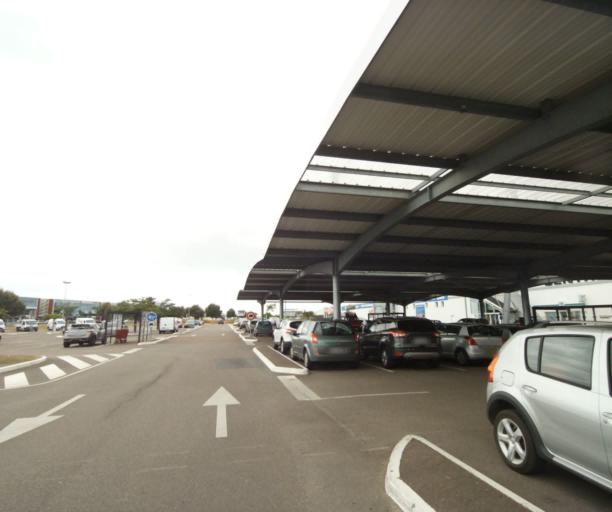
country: FR
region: Pays de la Loire
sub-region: Departement de la Vendee
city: Chateau-d'Olonne
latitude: 46.4938
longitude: -1.7492
